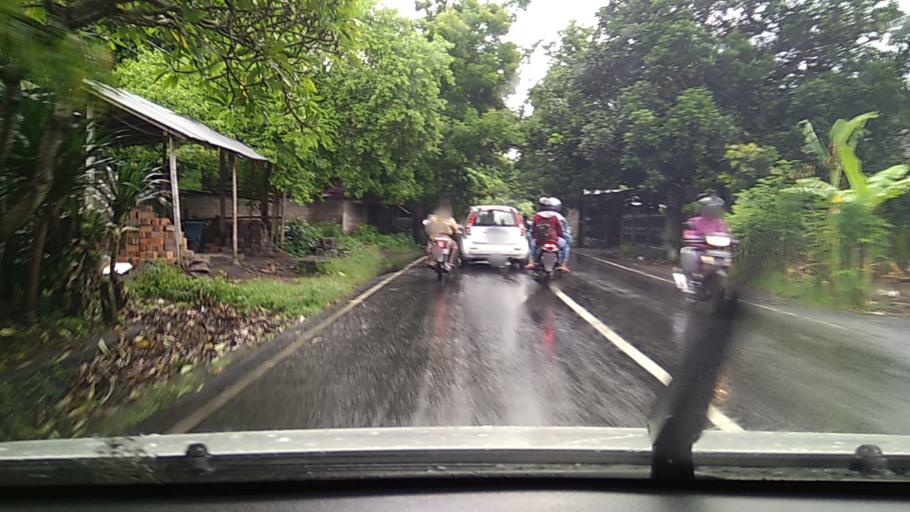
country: ID
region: Bali
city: Banjar Timbrah
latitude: -8.4825
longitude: 115.6069
